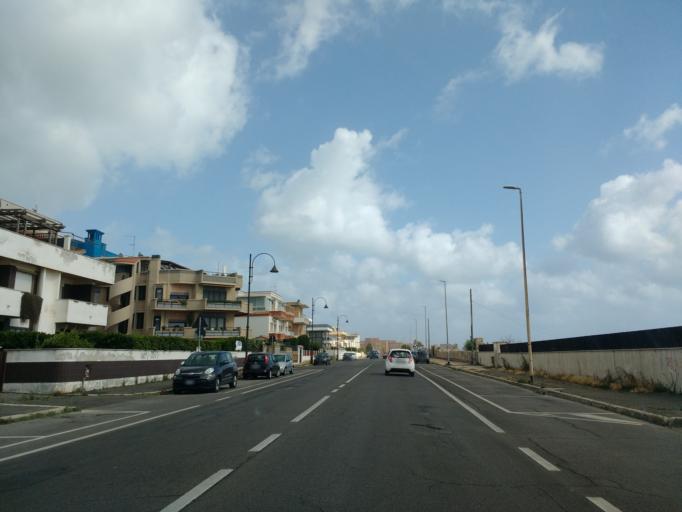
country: IT
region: Latium
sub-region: Citta metropolitana di Roma Capitale
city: Anzio
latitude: 41.4580
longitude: 12.6150
